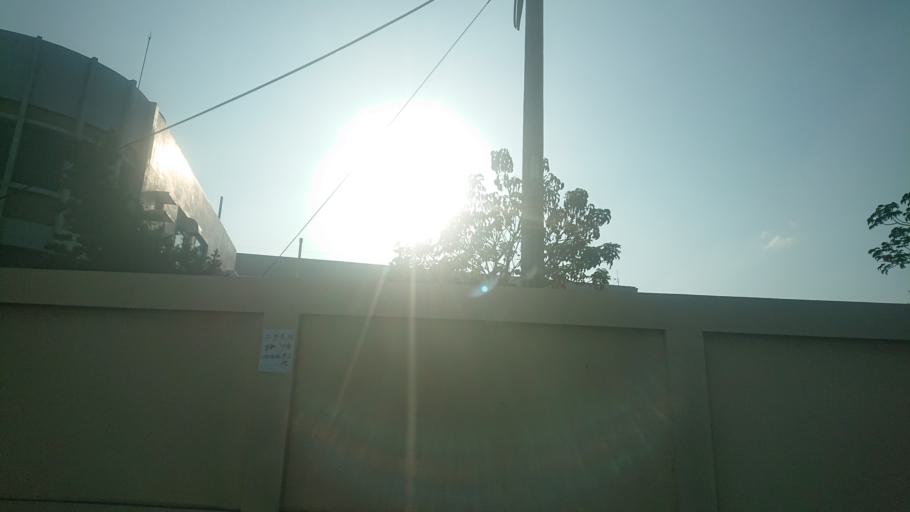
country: TW
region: Taiwan
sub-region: Tainan
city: Tainan
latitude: 23.0749
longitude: 120.2133
